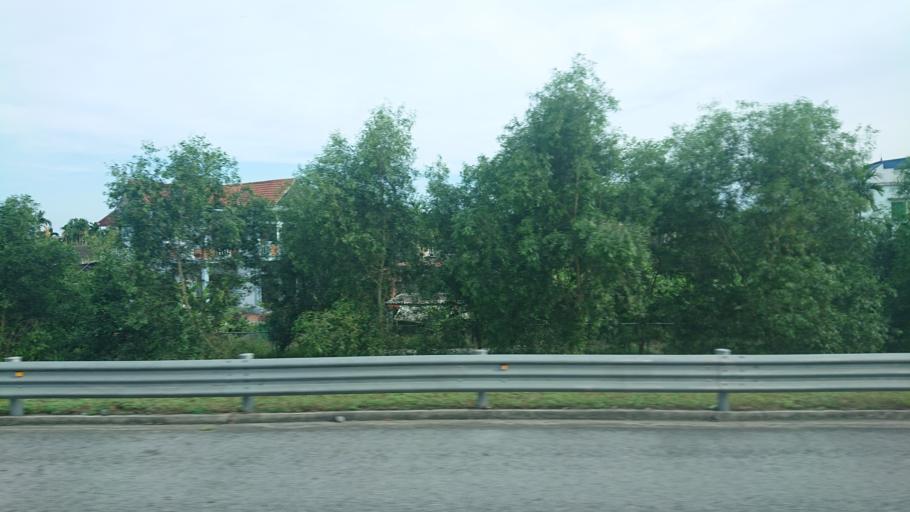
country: VN
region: Hai Phong
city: Nui Doi
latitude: 20.7654
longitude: 106.6676
